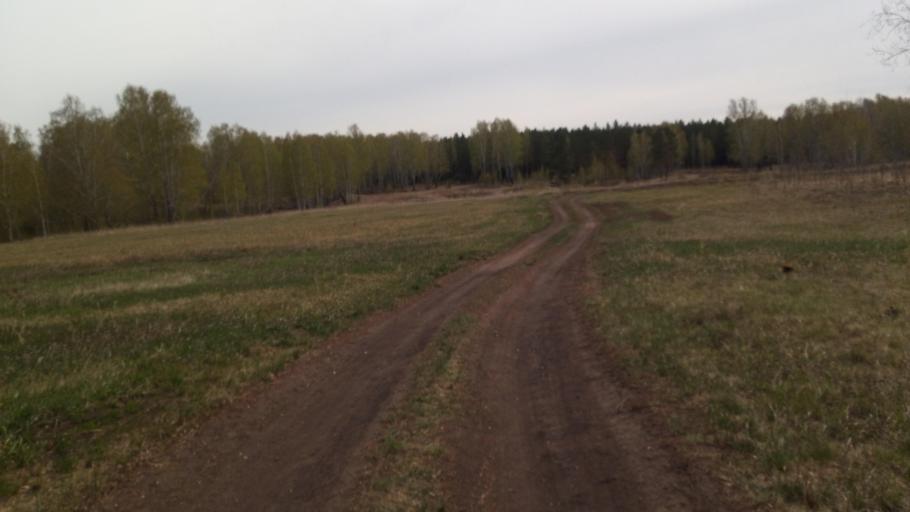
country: RU
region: Chelyabinsk
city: Timiryazevskiy
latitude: 55.0233
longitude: 60.8504
